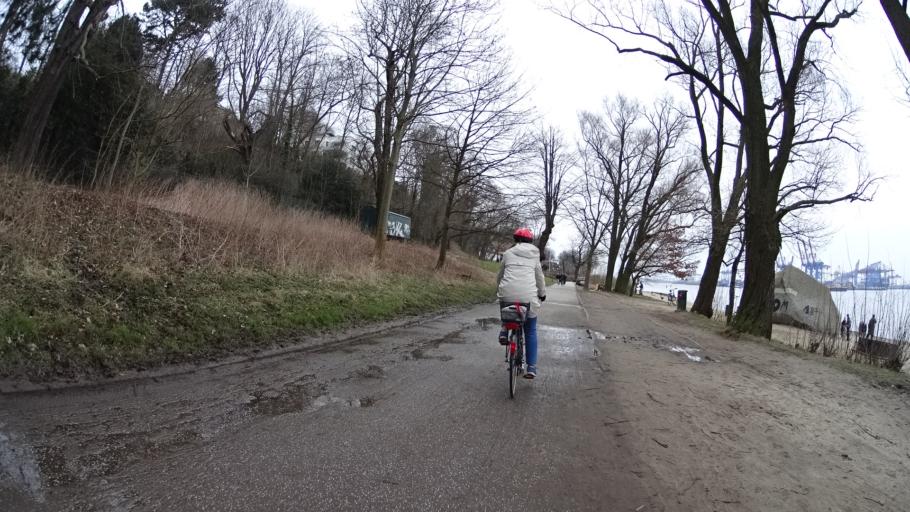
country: DE
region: Hamburg
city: Altona
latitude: 53.5448
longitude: 9.8951
